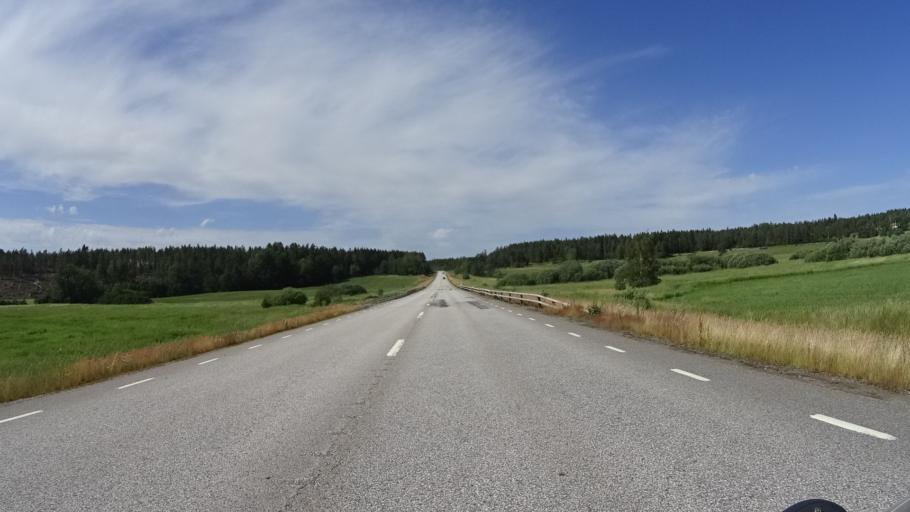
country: SE
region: Kalmar
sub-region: Vasterviks Kommun
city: Gamleby
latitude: 57.9457
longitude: 16.3825
